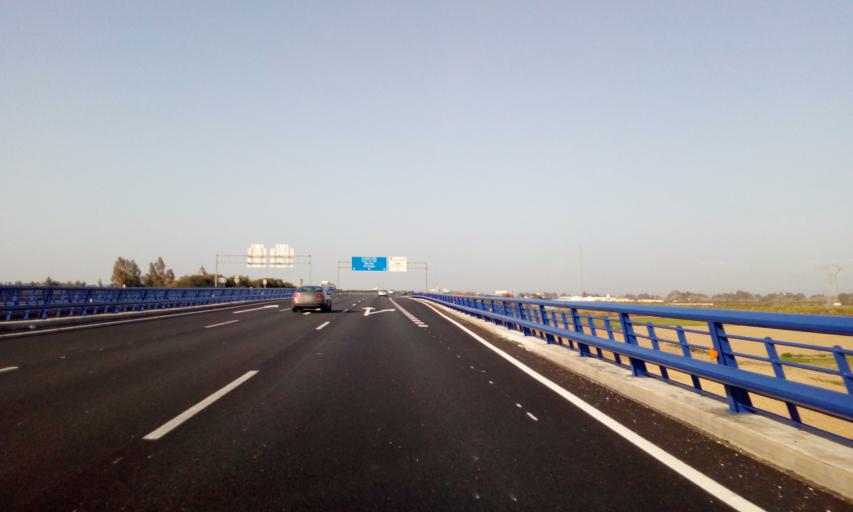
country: ES
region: Andalusia
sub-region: Provincia de Sevilla
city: Santiponce
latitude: 37.4266
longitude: -6.0301
